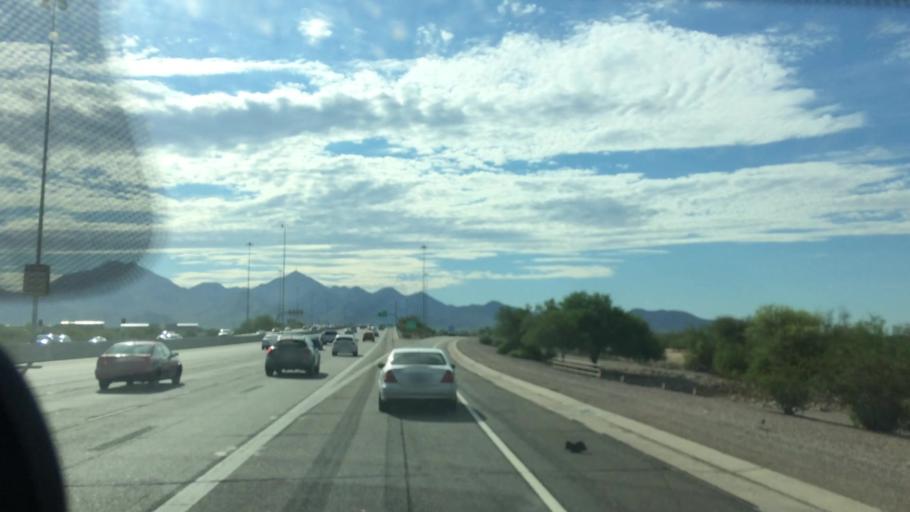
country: US
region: Arizona
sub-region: Maricopa County
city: Paradise Valley
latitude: 33.6555
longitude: -111.9143
